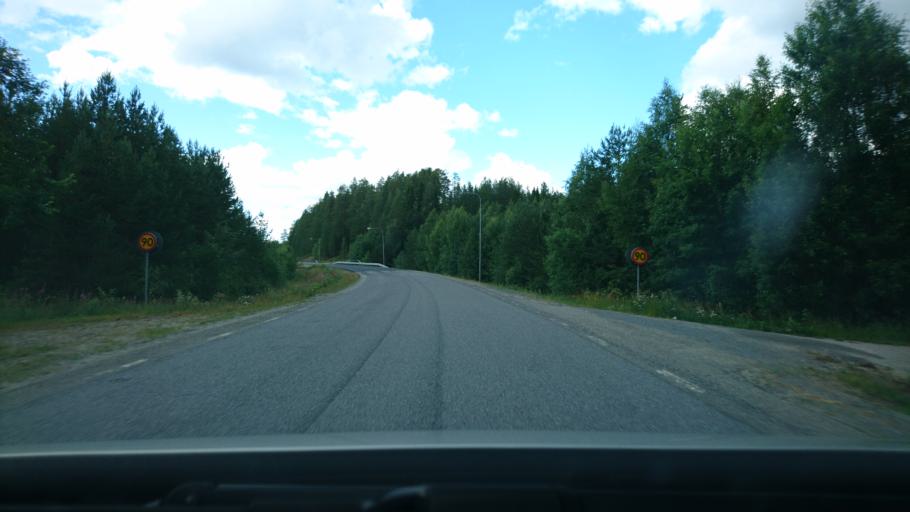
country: SE
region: Vaesterbotten
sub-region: Asele Kommun
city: Asele
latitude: 63.9426
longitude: 17.2830
